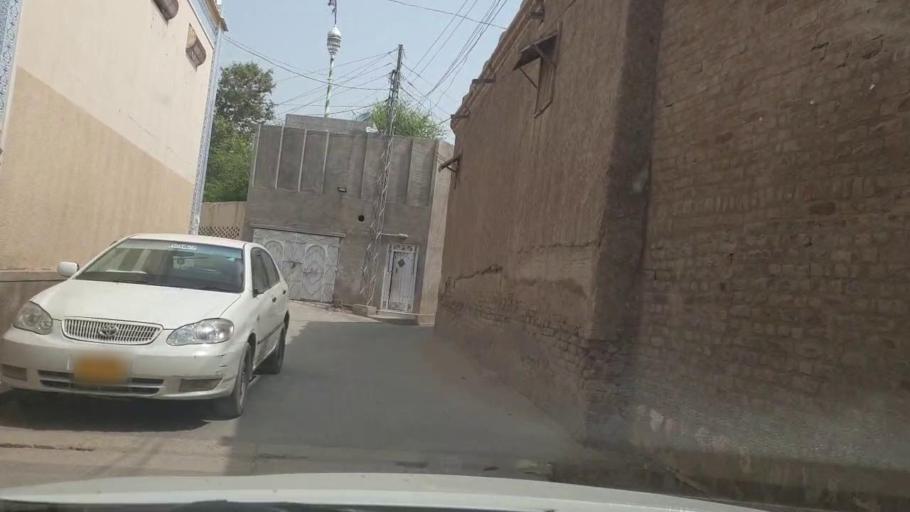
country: PK
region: Sindh
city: Kot Diji
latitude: 27.3401
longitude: 68.7081
